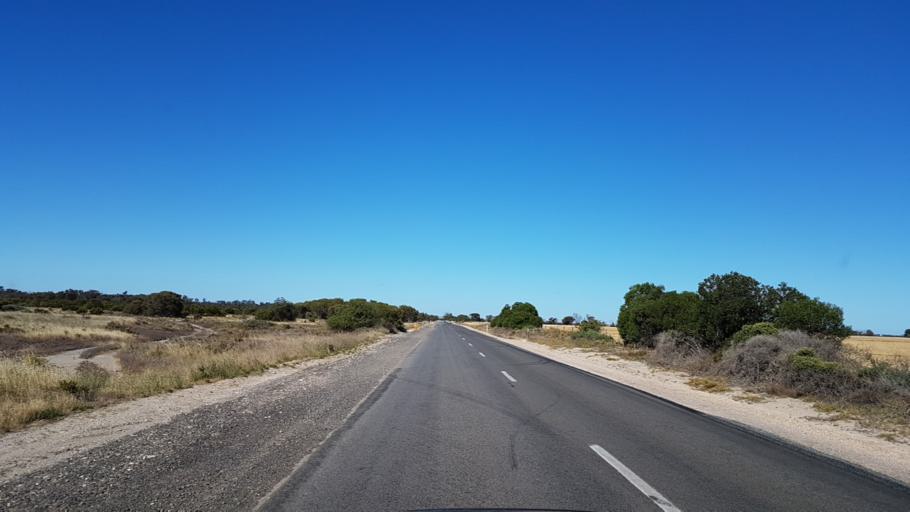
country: AU
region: South Australia
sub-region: Yorke Peninsula
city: Honiton
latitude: -34.9470
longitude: 137.4221
